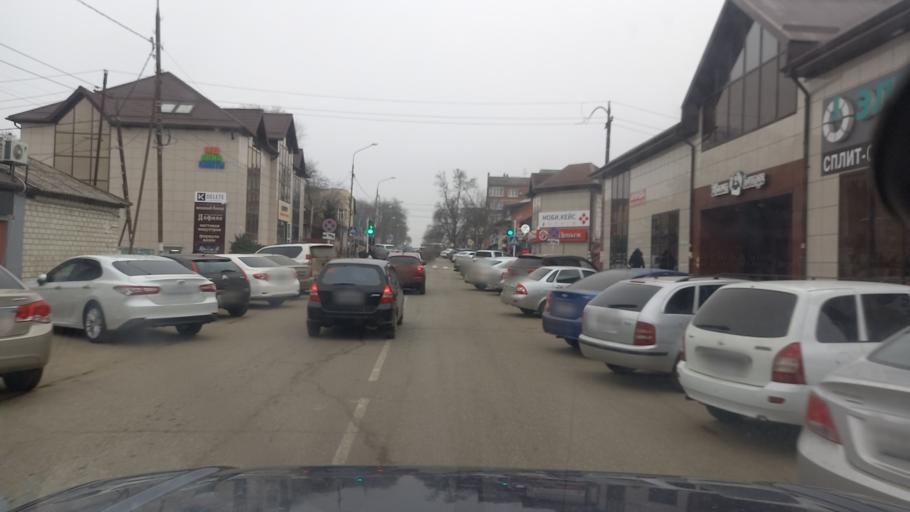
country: RU
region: Krasnodarskiy
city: Apsheronsk
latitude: 44.4644
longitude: 39.7400
